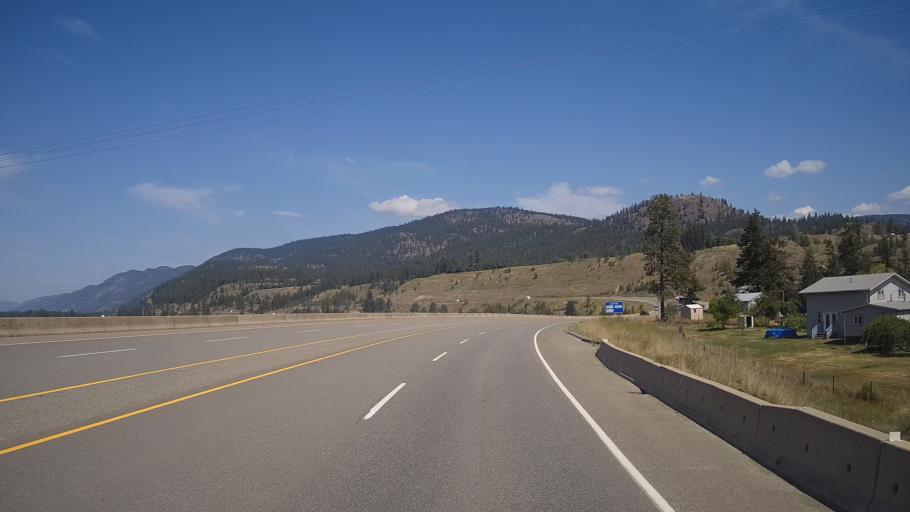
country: CA
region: British Columbia
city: Kamloops
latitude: 50.8596
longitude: -120.2716
